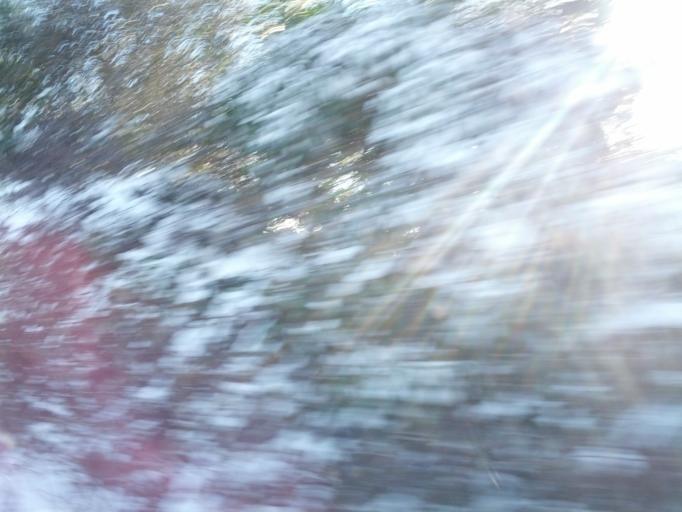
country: IE
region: Connaught
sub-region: County Galway
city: Athenry
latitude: 53.1945
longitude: -8.7952
